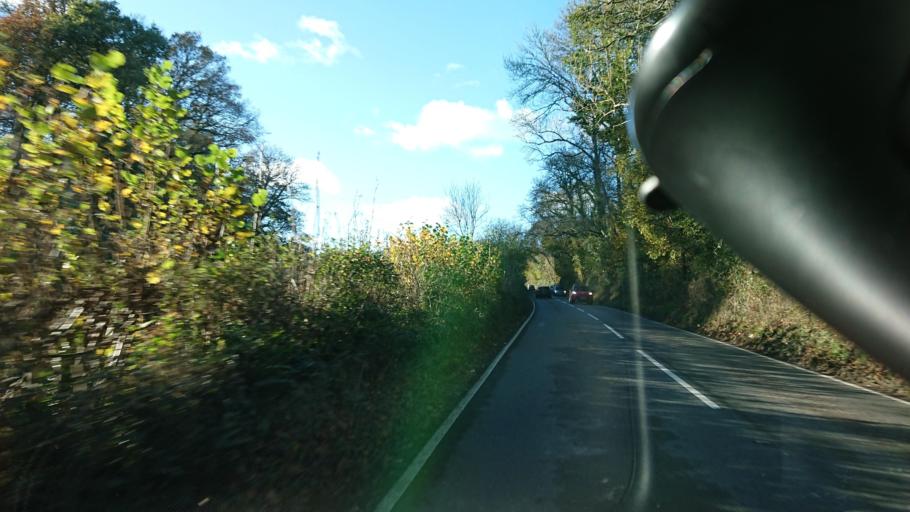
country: GB
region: England
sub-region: Cornwall
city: Pillaton
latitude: 50.3895
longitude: -4.3484
